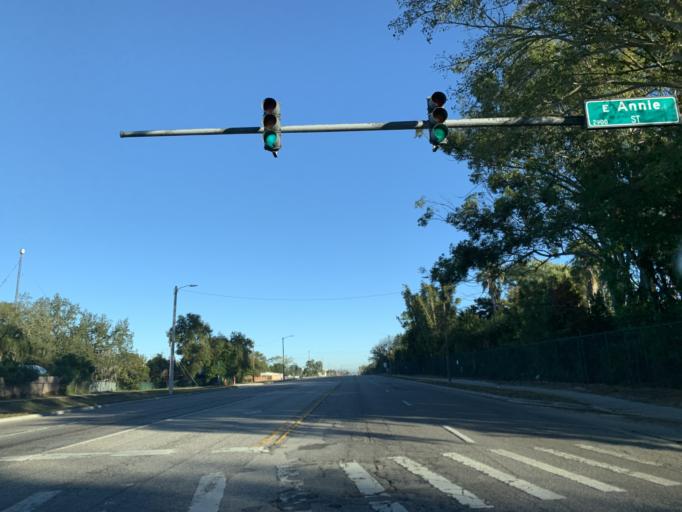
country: US
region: Florida
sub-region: Hillsborough County
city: University
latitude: 28.0363
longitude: -82.4262
